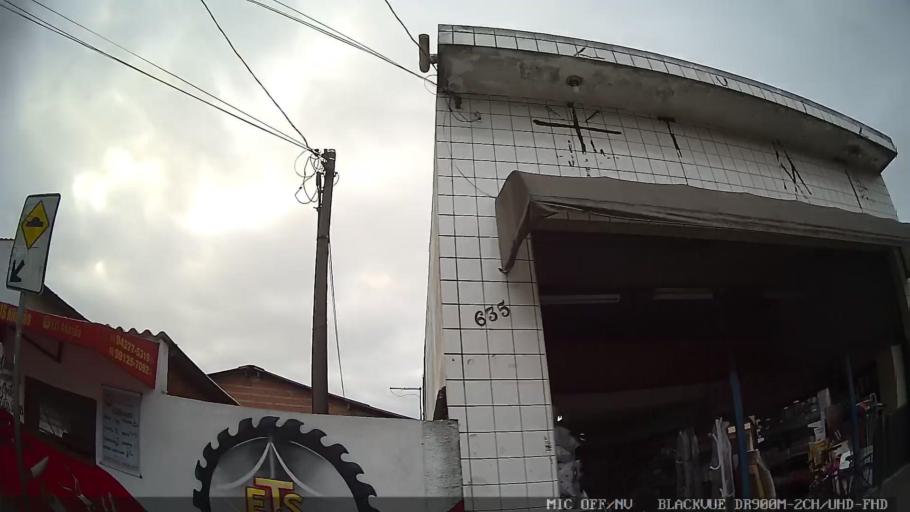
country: BR
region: Sao Paulo
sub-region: Itaquaquecetuba
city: Itaquaquecetuba
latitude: -23.4872
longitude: -46.3908
